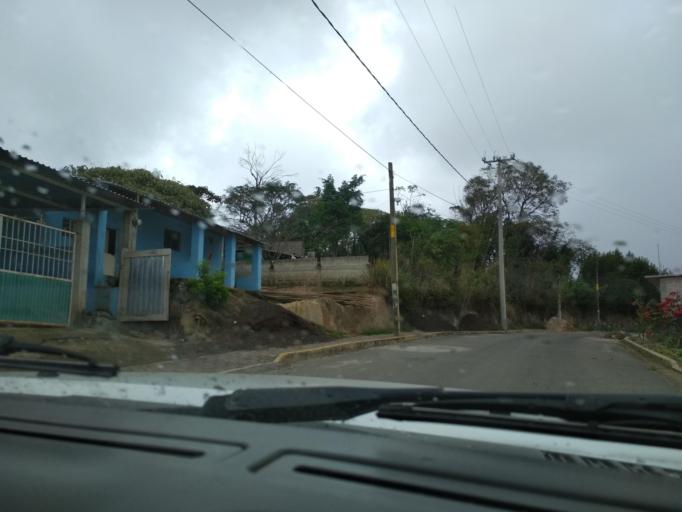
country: MX
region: Veracruz
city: El Castillo
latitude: 19.5413
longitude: -96.8254
